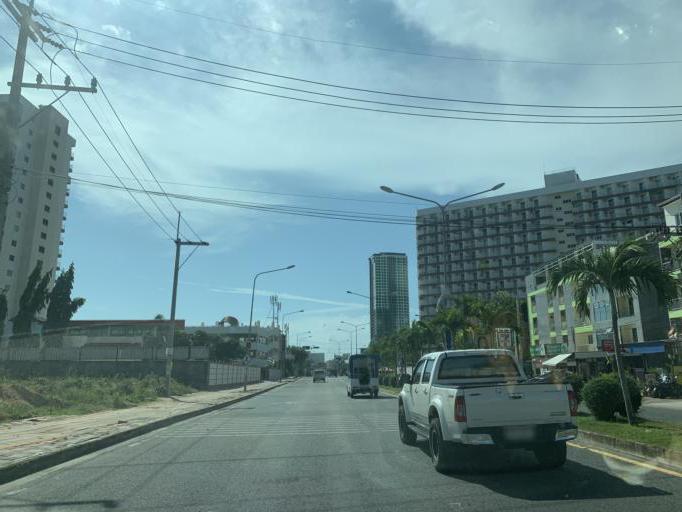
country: TH
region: Chon Buri
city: Phatthaya
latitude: 12.8895
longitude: 100.8802
